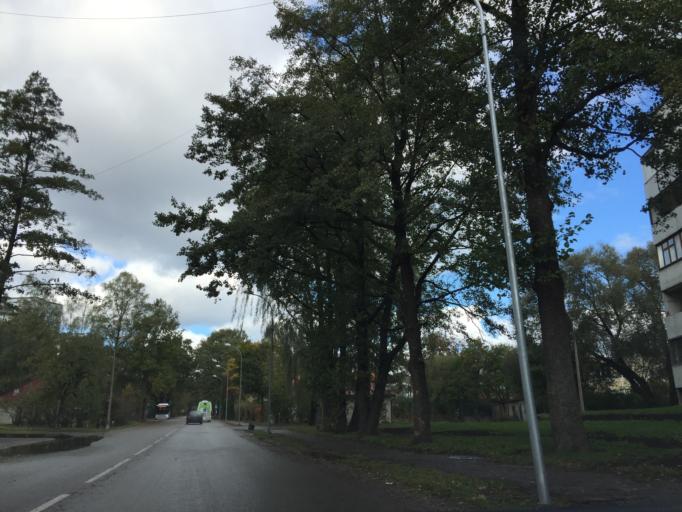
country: LV
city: Tireli
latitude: 56.9511
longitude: 23.6110
